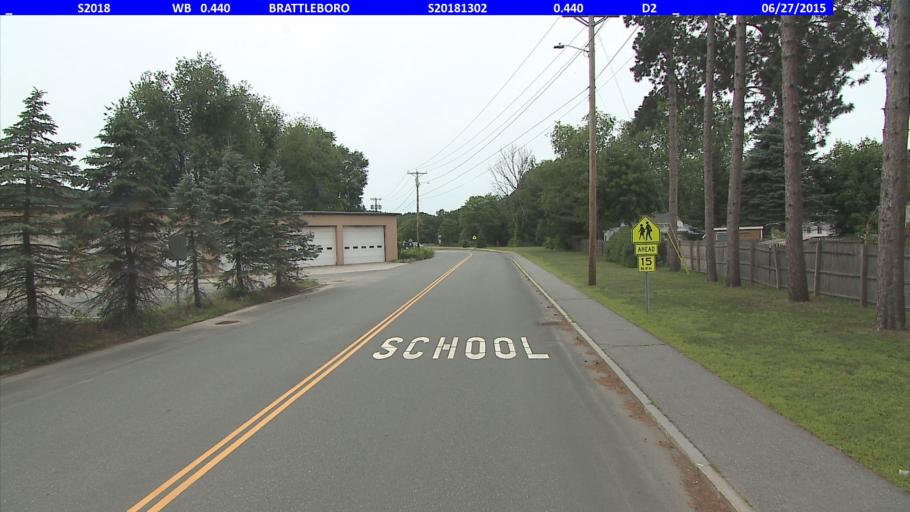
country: US
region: Vermont
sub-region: Windham County
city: Brattleboro
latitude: 42.8373
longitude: -72.5575
